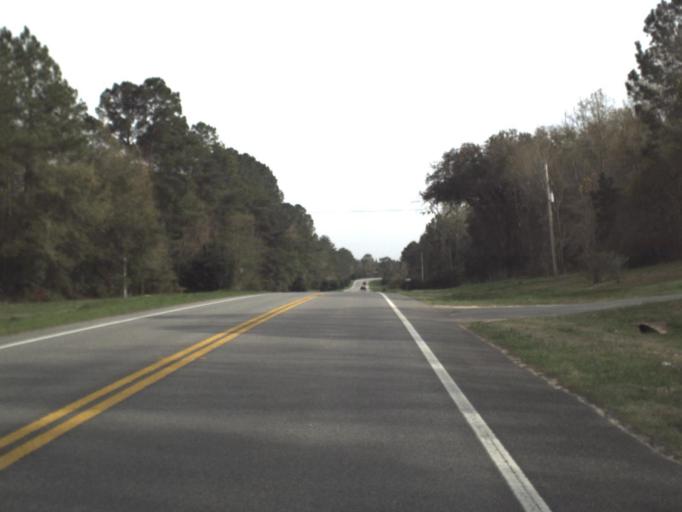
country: US
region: Florida
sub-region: Jefferson County
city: Monticello
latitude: 30.5391
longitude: -83.8363
